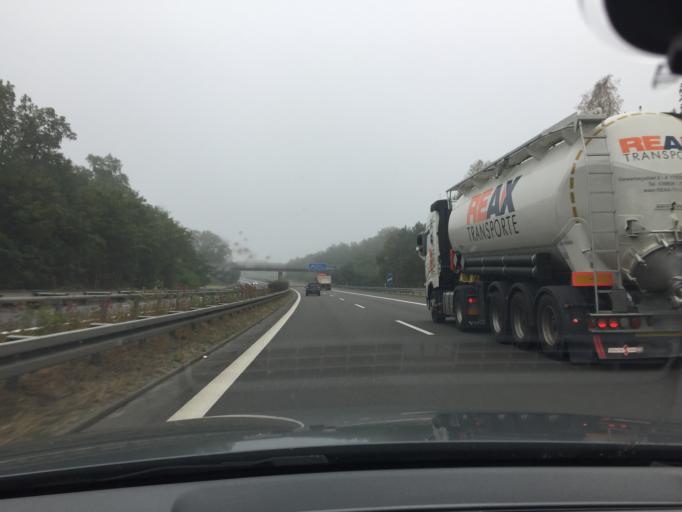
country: DE
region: Brandenburg
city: Bronkow
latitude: 51.6660
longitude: 13.9077
